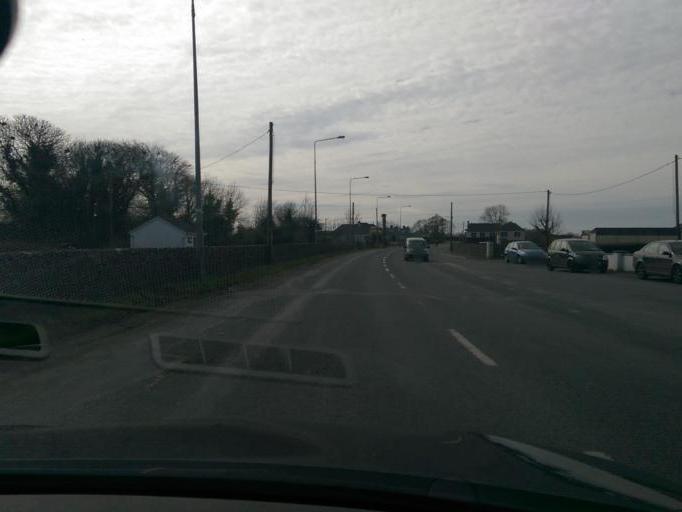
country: IE
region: Connaught
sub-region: County Galway
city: Claregalway
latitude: 53.3818
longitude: -8.8542
